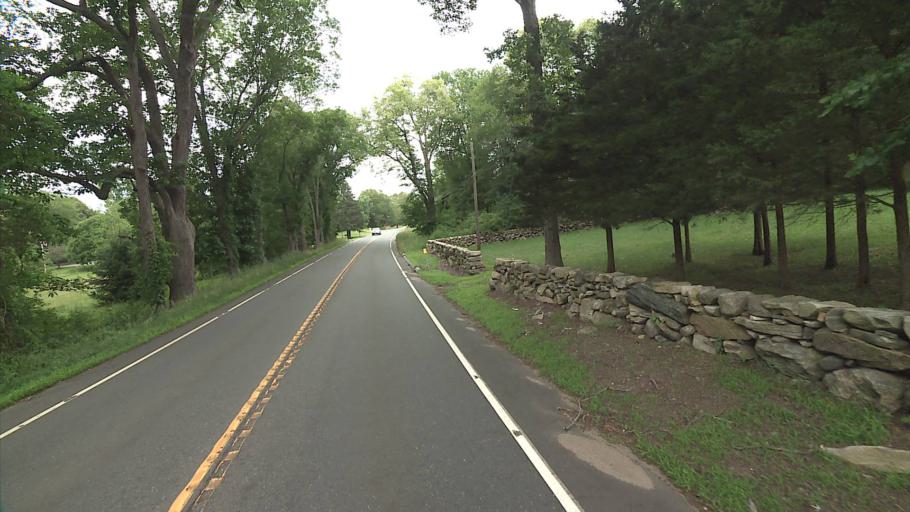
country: US
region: Connecticut
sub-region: New London County
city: Ledyard Center
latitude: 41.4765
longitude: -72.0323
